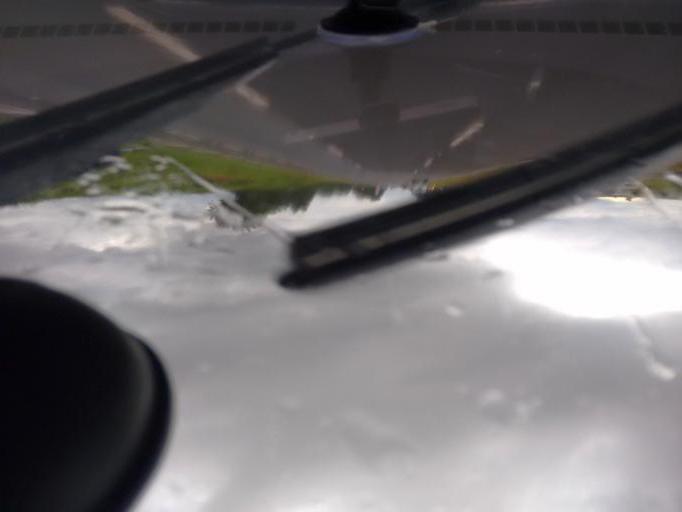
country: BR
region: Sao Paulo
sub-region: Nova Odessa
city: Nova Odessa
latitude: -22.8339
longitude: -47.3566
